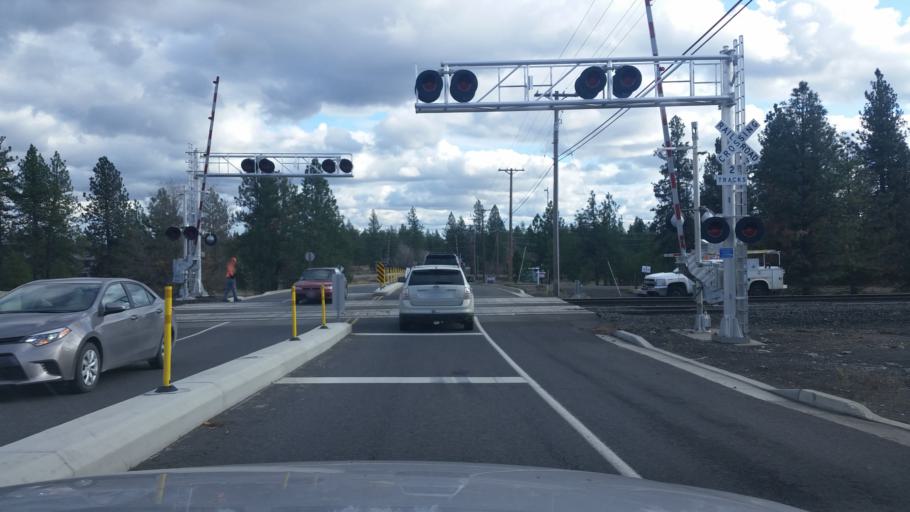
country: US
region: Washington
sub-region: Spokane County
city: Cheney
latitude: 47.4823
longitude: -117.5817
